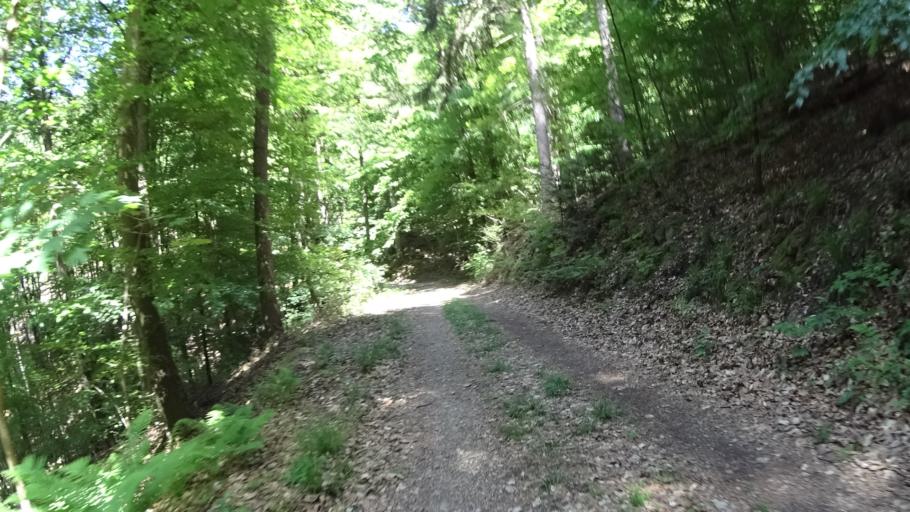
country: DE
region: Baden-Wuerttemberg
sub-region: Karlsruhe Region
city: Neckargemund
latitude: 49.4056
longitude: 8.7860
